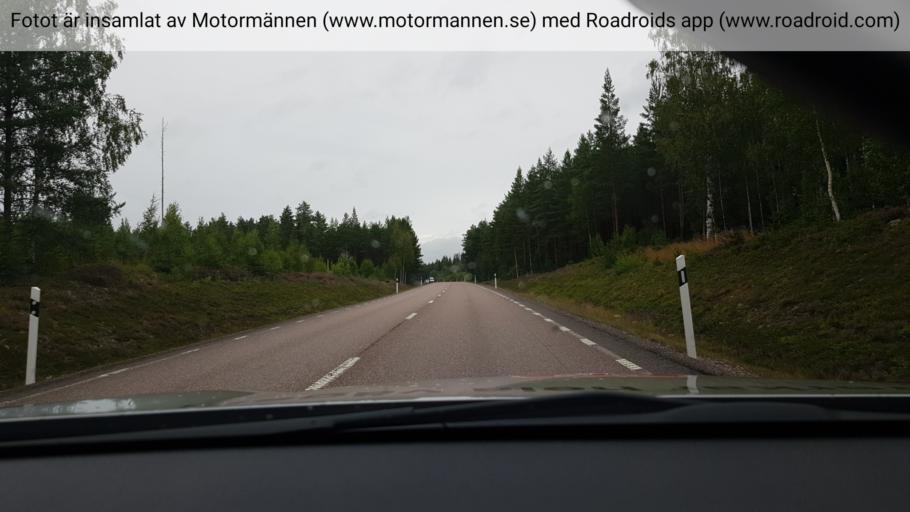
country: SE
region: Gaevleborg
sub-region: Gavle Kommun
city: Hedesunda
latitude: 60.3511
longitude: 16.9598
